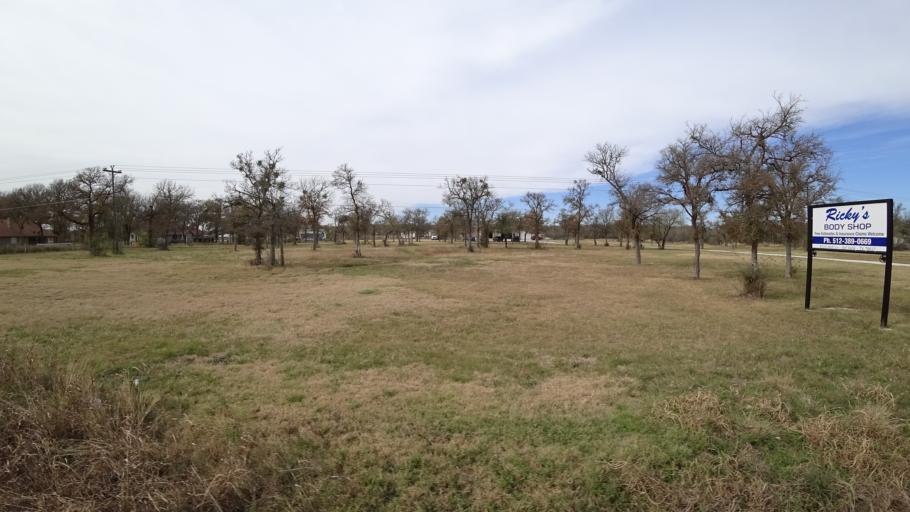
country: US
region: Texas
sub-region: Travis County
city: Garfield
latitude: 30.1331
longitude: -97.5723
